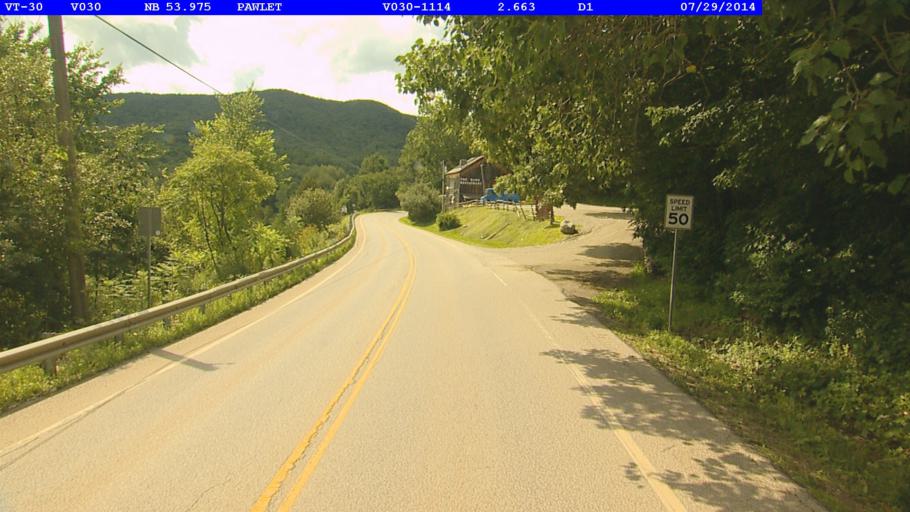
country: US
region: New York
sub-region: Washington County
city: Granville
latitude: 43.3474
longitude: -73.1795
